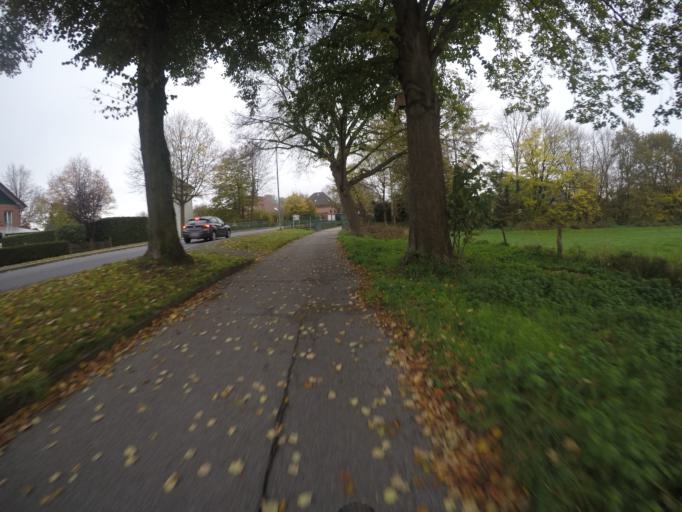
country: DE
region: North Rhine-Westphalia
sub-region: Regierungsbezirk Munster
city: Isselburg
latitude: 51.8220
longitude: 6.5118
